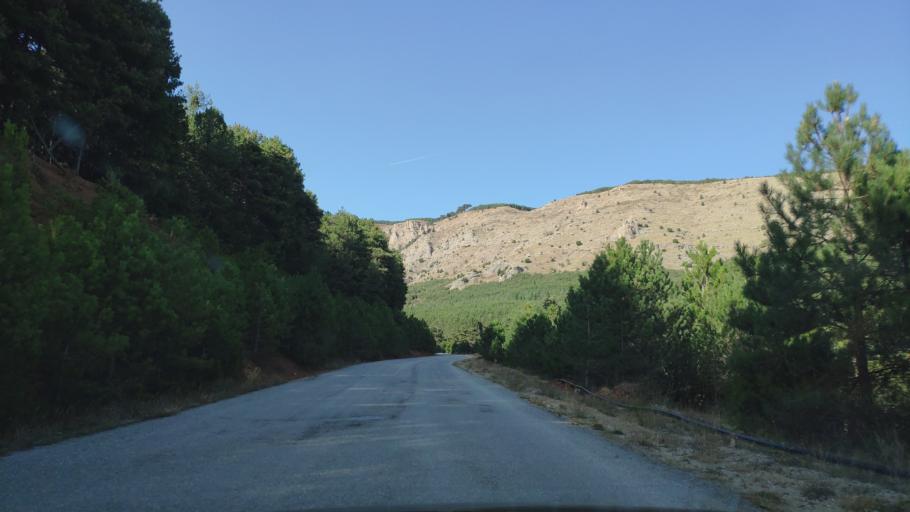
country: GR
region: West Greece
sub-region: Nomos Achaias
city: Aiyira
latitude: 38.0282
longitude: 22.4033
